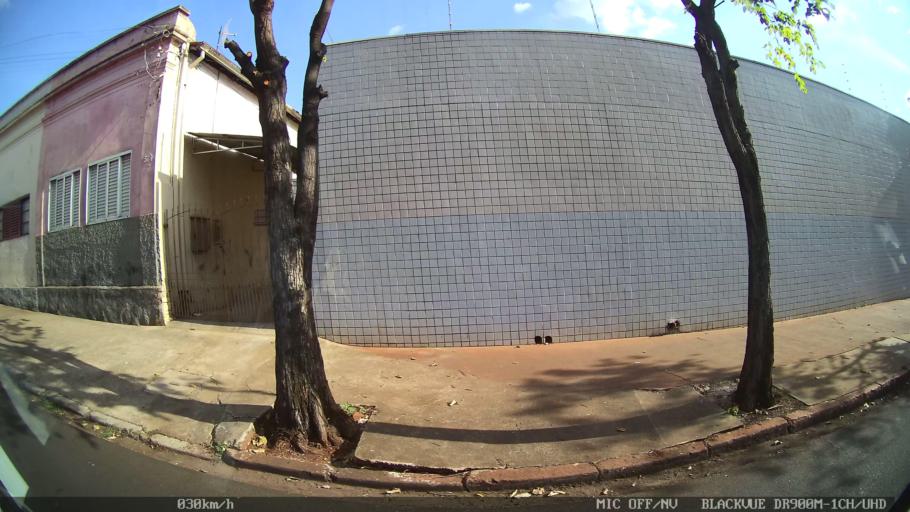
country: BR
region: Sao Paulo
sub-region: Ribeirao Preto
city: Ribeirao Preto
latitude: -21.1636
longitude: -47.8098
